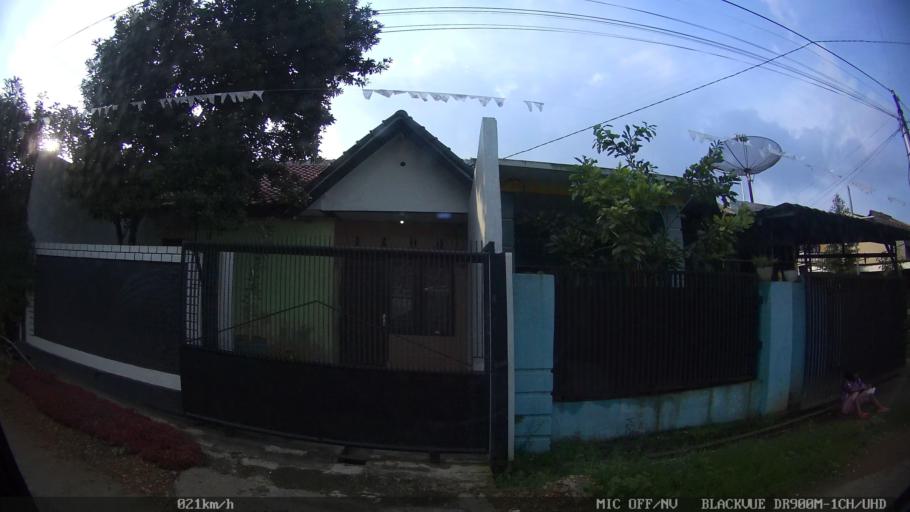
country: ID
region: Lampung
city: Panjang
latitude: -5.4020
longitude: 105.3508
